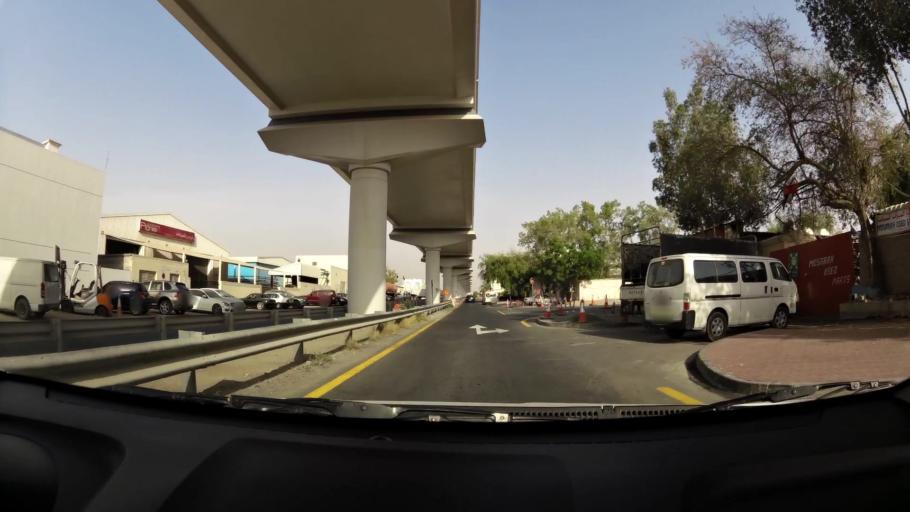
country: AE
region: Ash Shariqah
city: Sharjah
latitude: 25.2384
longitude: 55.3709
